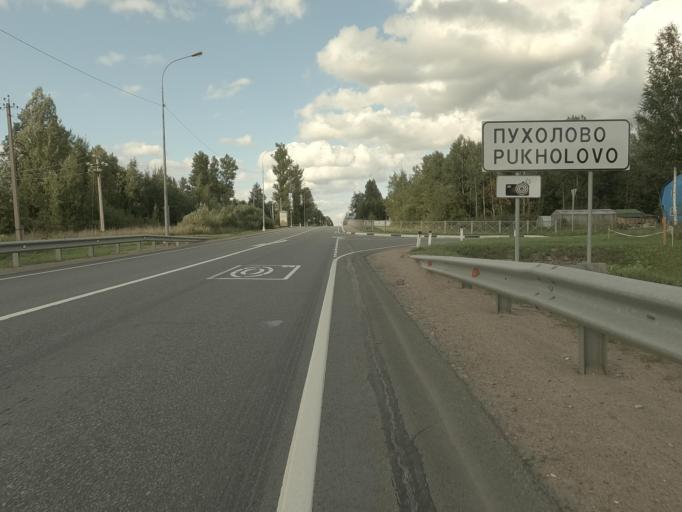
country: RU
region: Leningrad
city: Mga
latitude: 59.7334
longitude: 31.0675
